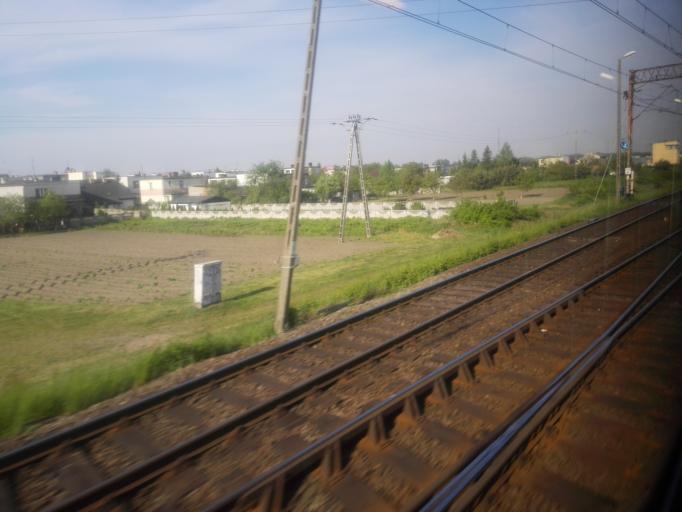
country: PL
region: Greater Poland Voivodeship
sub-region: Powiat wrzesinski
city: Wrzesnia
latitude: 52.3380
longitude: 17.5765
